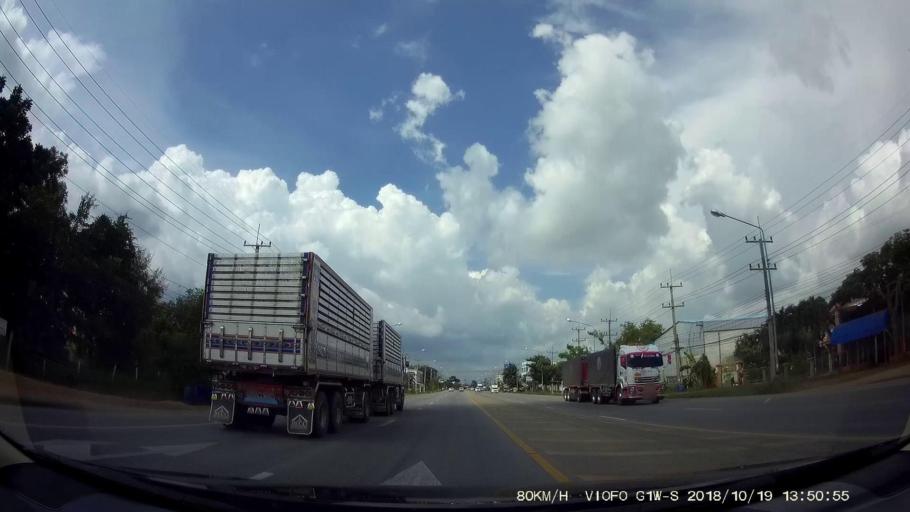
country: TH
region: Chaiyaphum
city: Chaiyaphum
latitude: 15.7500
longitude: 102.0240
